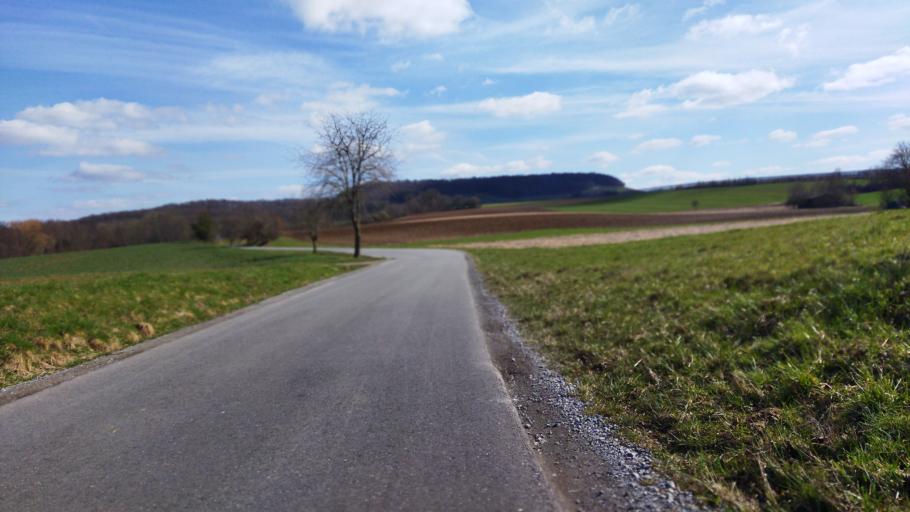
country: DE
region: Baden-Wuerttemberg
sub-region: Regierungsbezirk Stuttgart
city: Bretzfeld
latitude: 49.1724
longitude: 9.4469
